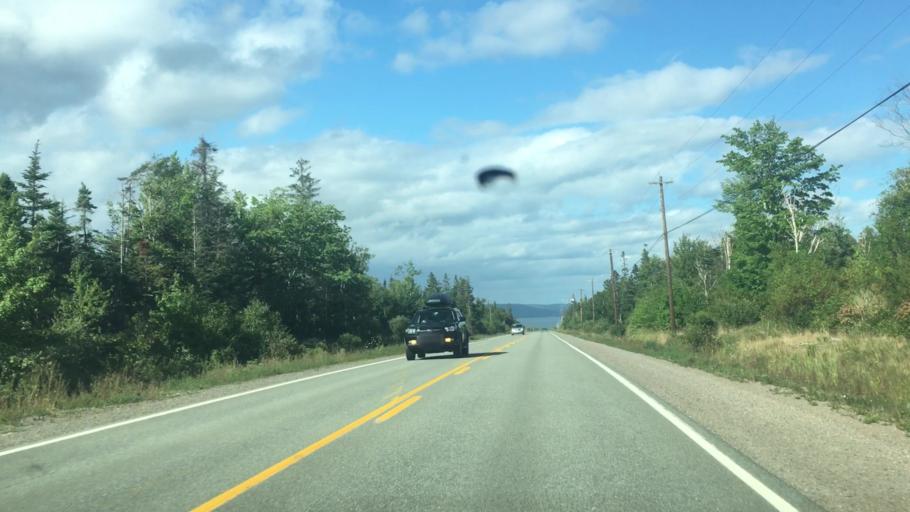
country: CA
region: Nova Scotia
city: Sydney
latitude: 45.8571
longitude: -60.6291
